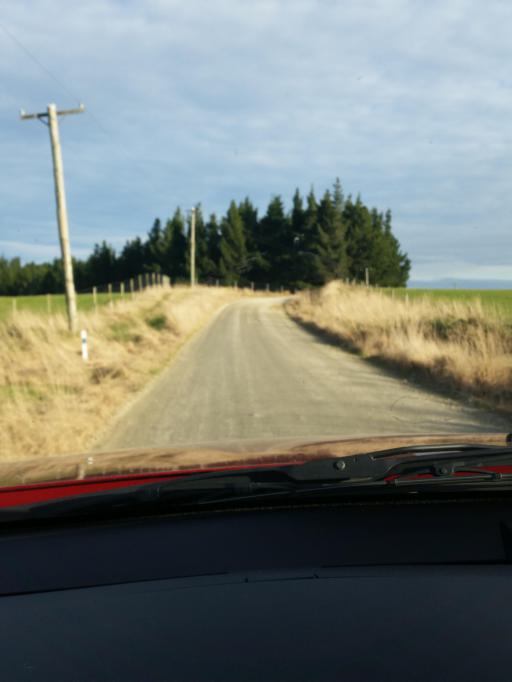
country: NZ
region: Southland
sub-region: Gore District
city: Gore
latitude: -46.2365
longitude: 168.7643
